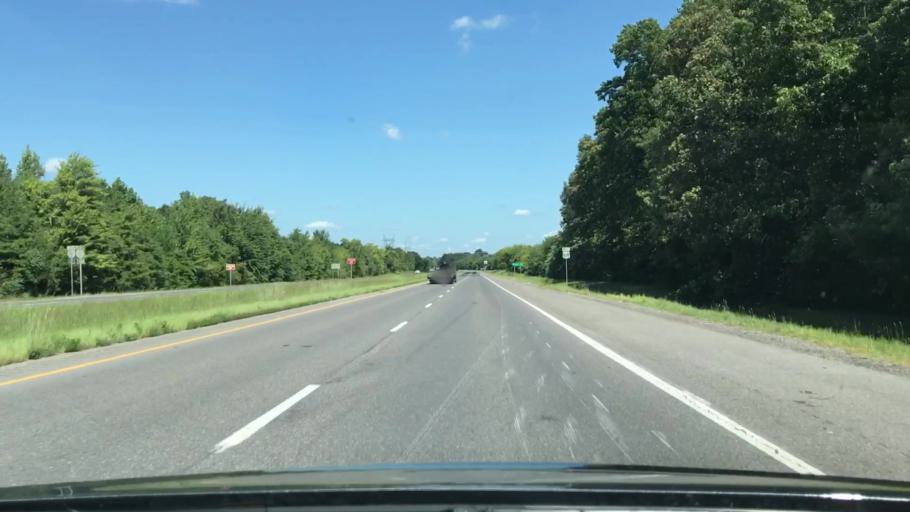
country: US
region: Kentucky
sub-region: McCracken County
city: Reidland
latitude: 36.9964
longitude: -88.5061
